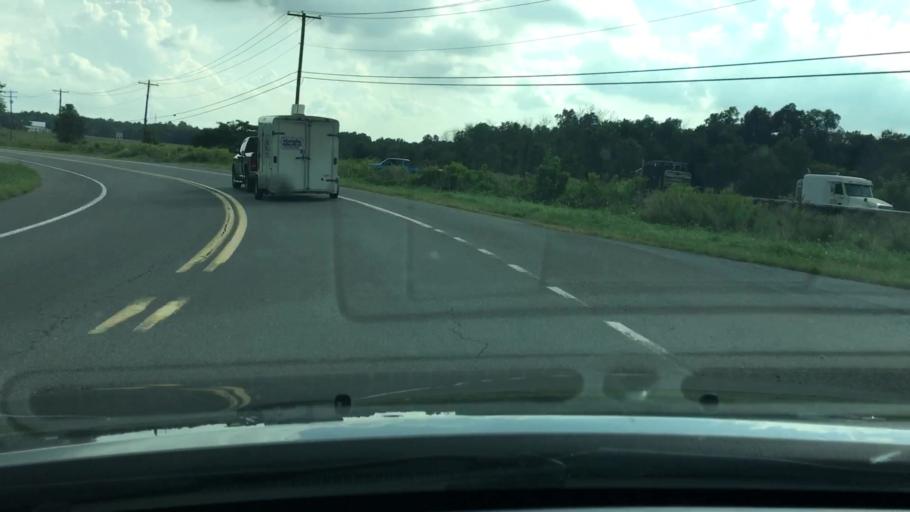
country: US
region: Pennsylvania
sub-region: Franklin County
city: Scotland
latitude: 39.9501
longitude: -77.5841
